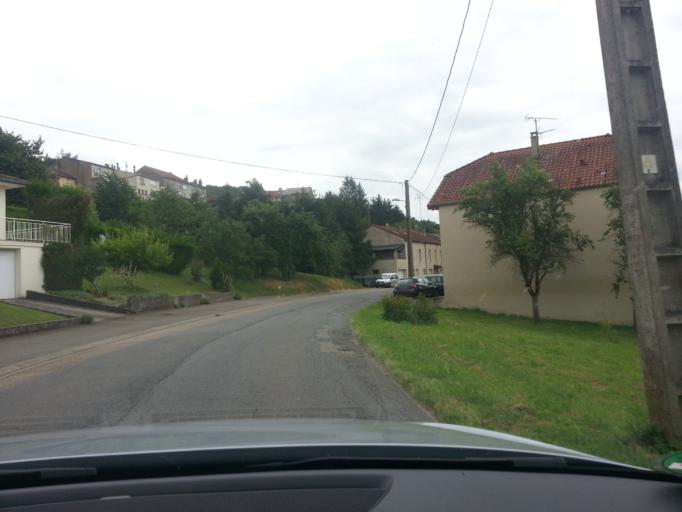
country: FR
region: Lorraine
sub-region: Departement de la Moselle
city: Sierck-les-Bains
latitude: 49.4540
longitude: 6.3434
